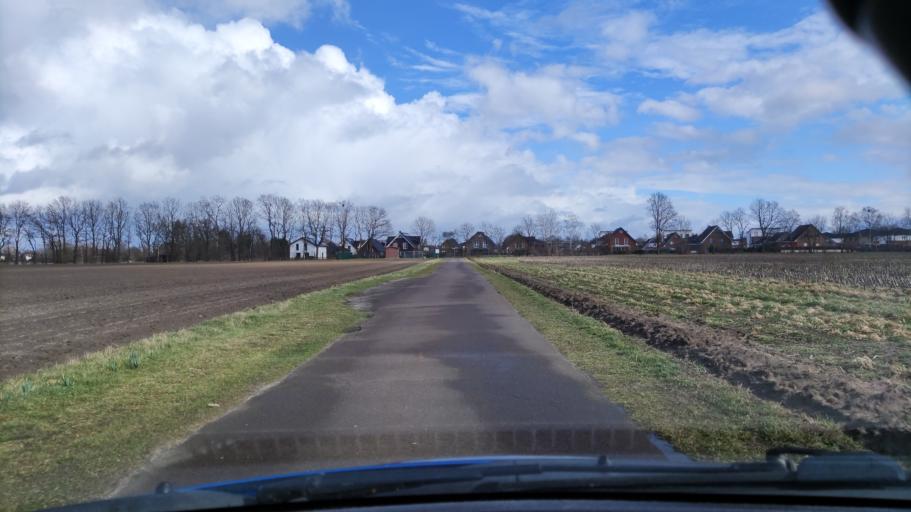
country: DE
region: Lower Saxony
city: Winsen
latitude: 53.3697
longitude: 10.1828
